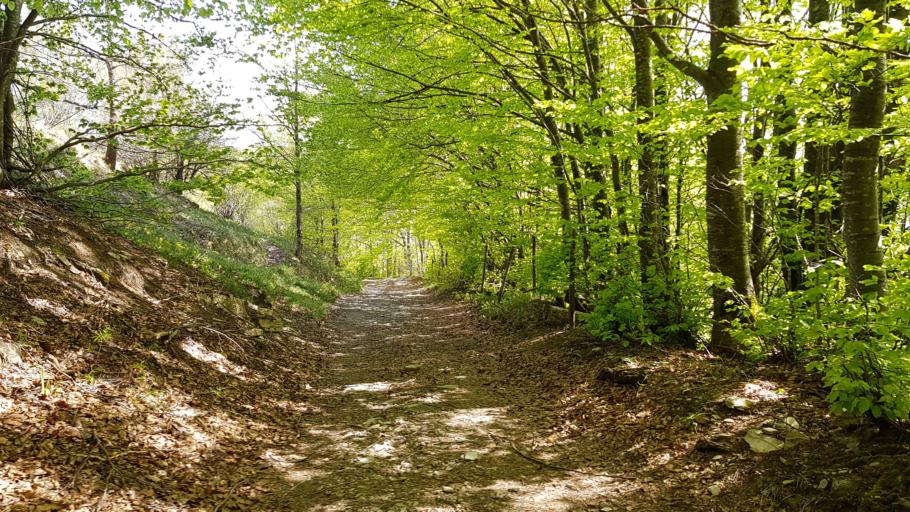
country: IT
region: Liguria
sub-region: Provincia di Genova
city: Fascia
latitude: 44.6037
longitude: 9.2044
